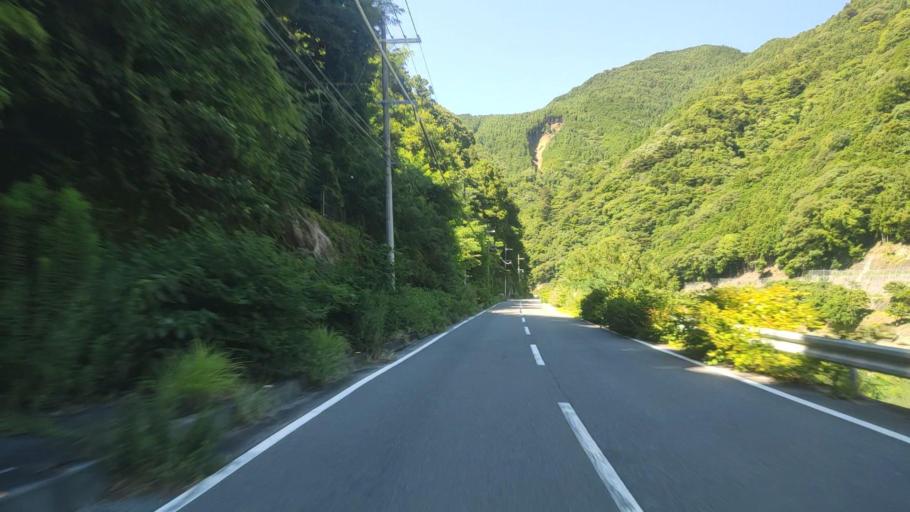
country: JP
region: Nara
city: Yoshino-cho
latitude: 34.3143
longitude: 135.9773
